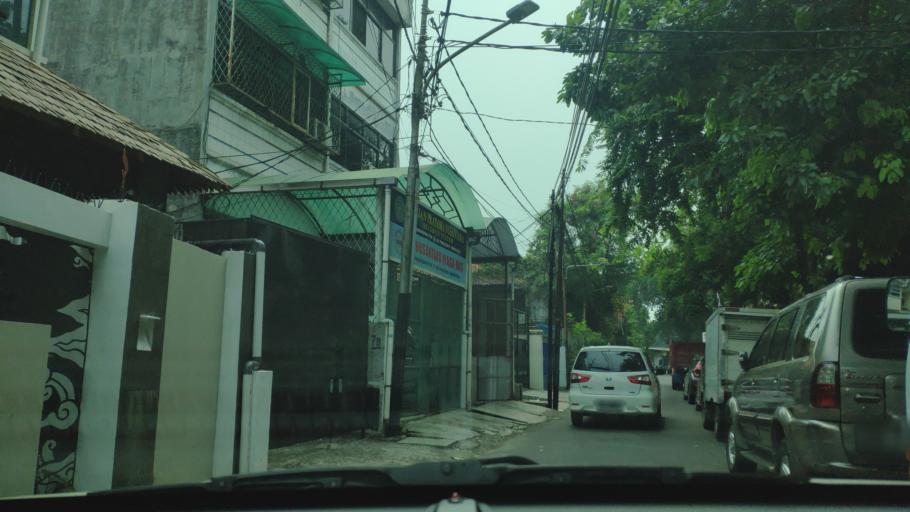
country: ID
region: Jakarta Raya
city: Jakarta
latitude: -6.1625
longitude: 106.8182
